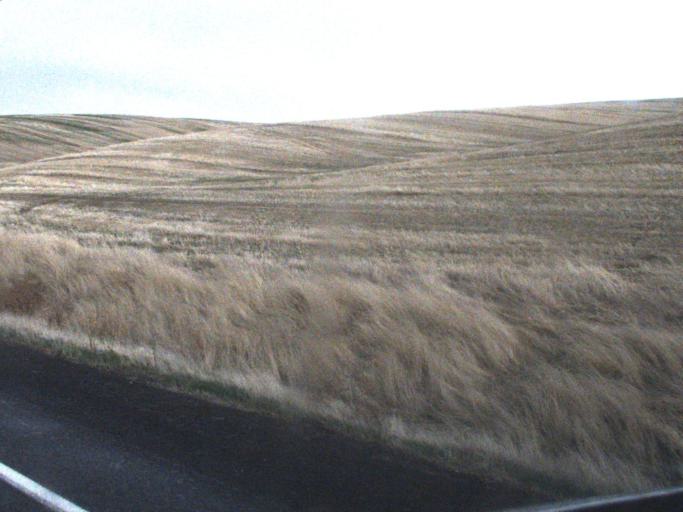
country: US
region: Washington
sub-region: Walla Walla County
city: Waitsburg
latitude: 46.1933
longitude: -118.1376
